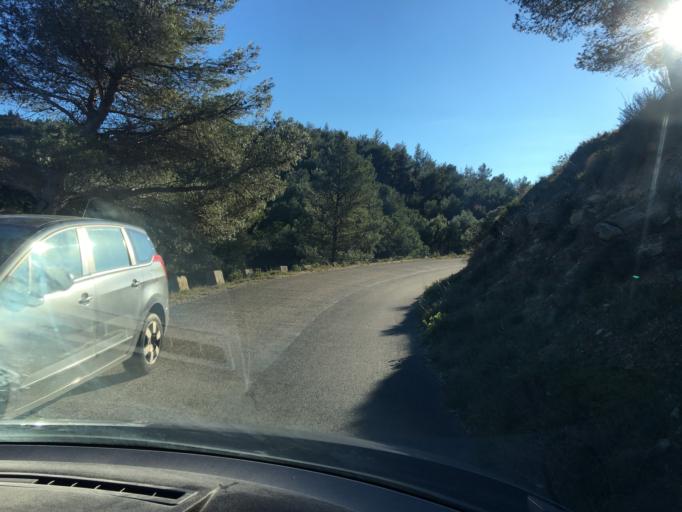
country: FR
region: Provence-Alpes-Cote d'Azur
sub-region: Departement des Bouches-du-Rhone
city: Maussane-les-Alpilles
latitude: 43.7557
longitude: 4.7931
